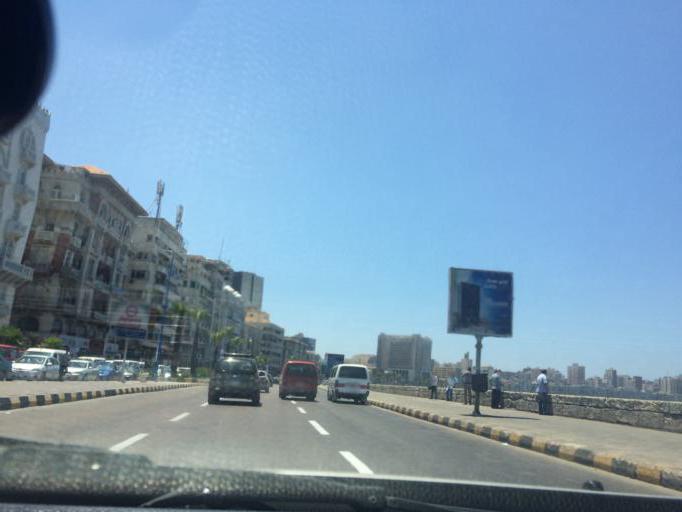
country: EG
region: Alexandria
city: Alexandria
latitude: 31.2014
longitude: 29.8989
